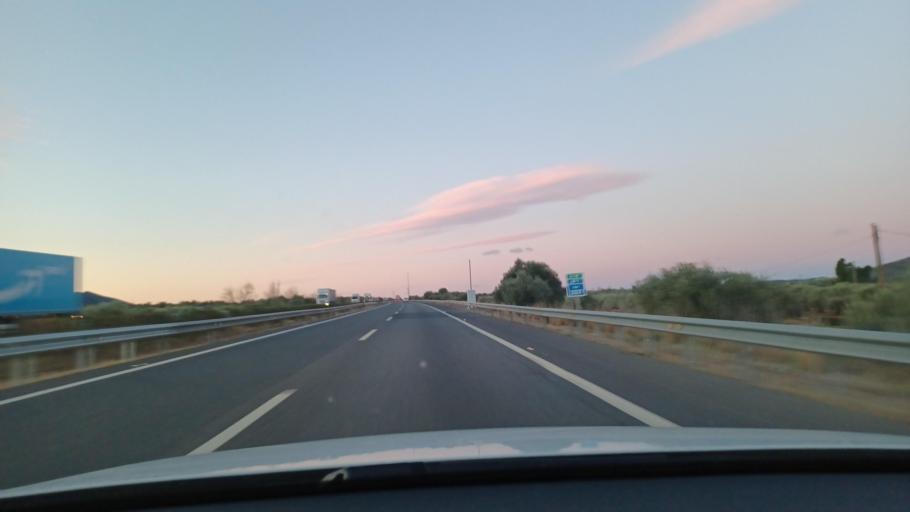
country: ES
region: Catalonia
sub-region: Provincia de Tarragona
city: Ulldecona
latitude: 40.6278
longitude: 0.4917
